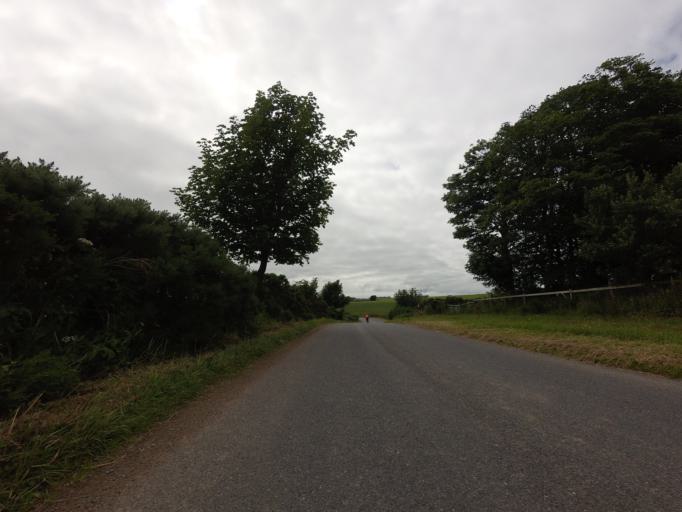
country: GB
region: Scotland
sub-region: Aberdeenshire
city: Turriff
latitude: 57.5432
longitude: -2.2616
